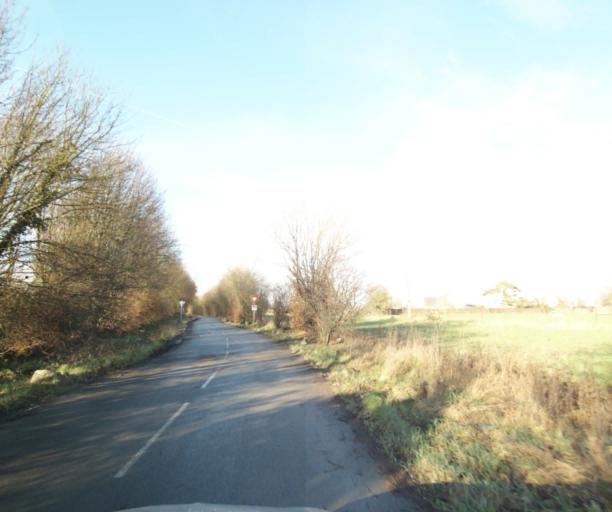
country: FR
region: Nord-Pas-de-Calais
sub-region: Departement du Nord
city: Curgies
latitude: 50.3226
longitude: 3.6007
